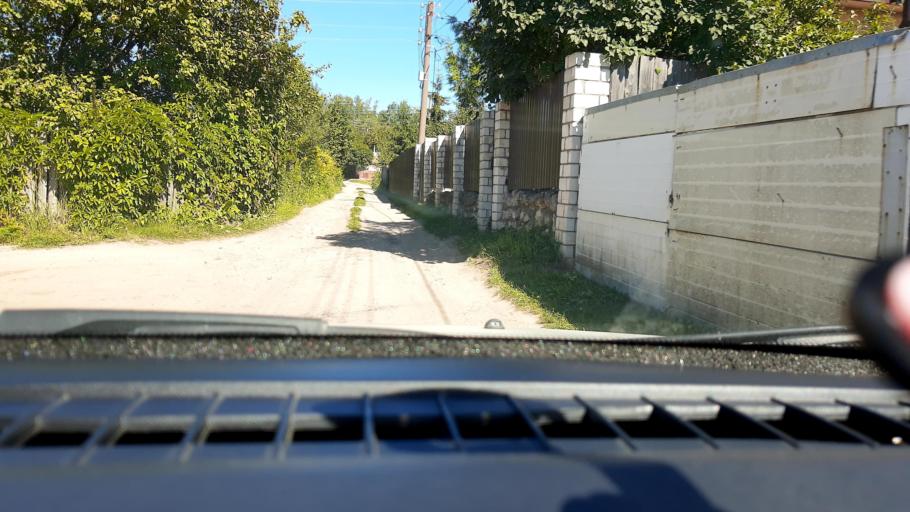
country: RU
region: Nizjnij Novgorod
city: Afonino
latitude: 56.2099
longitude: 44.1277
